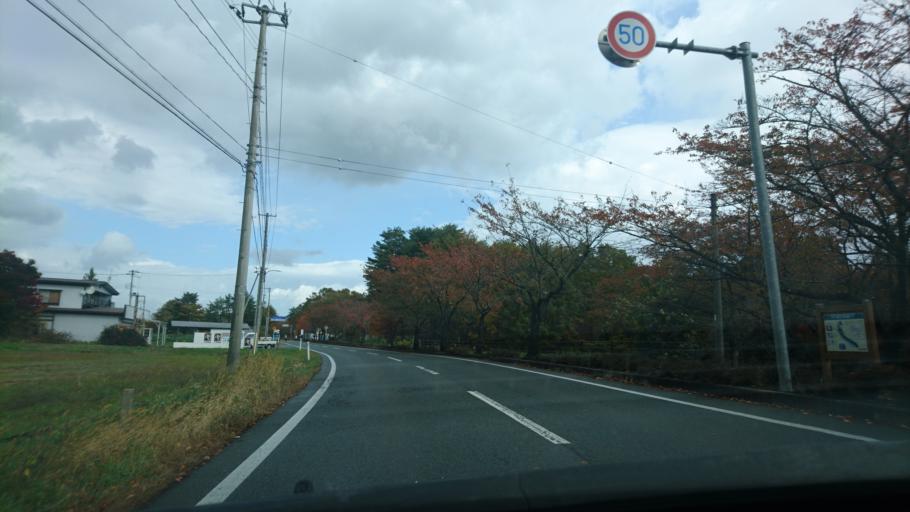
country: JP
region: Iwate
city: Shizukuishi
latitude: 39.6858
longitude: 141.0215
